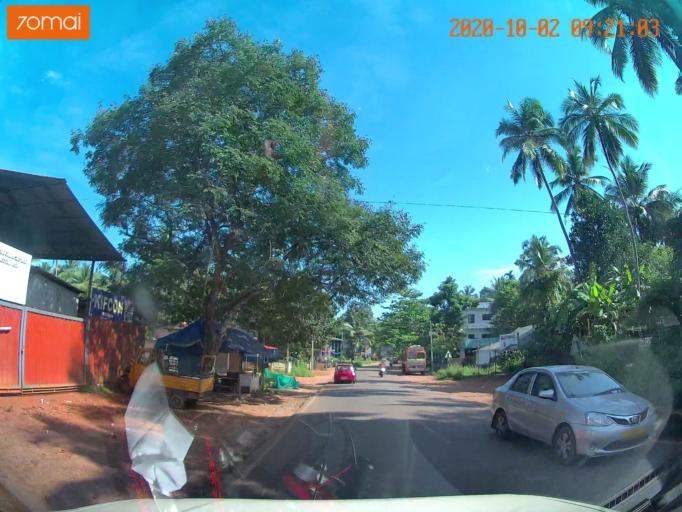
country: IN
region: Kerala
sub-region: Kozhikode
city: Naduvannur
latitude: 11.5709
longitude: 75.7537
